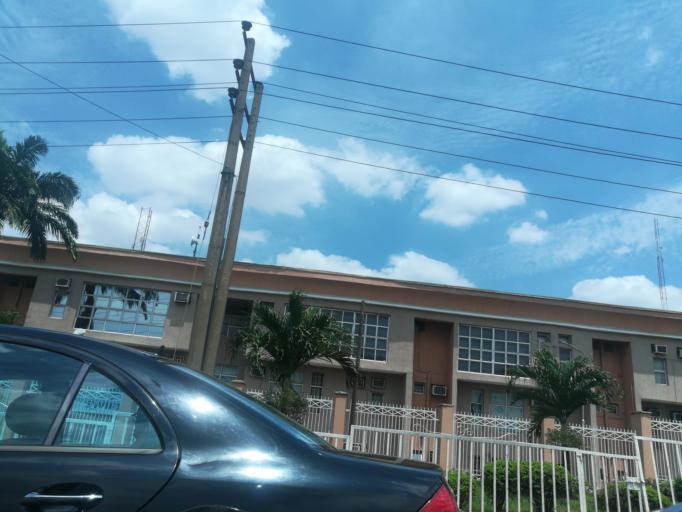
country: NG
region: Lagos
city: Ikeja
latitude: 6.6109
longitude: 3.3533
